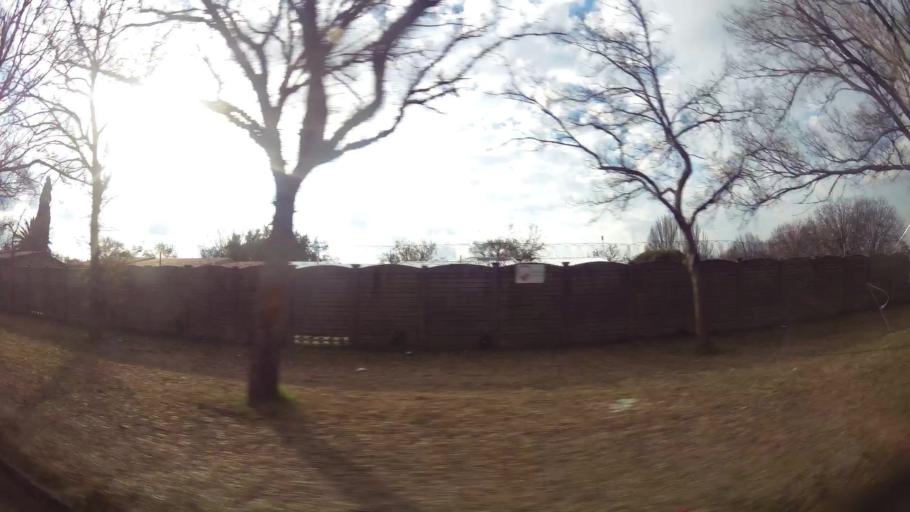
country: ZA
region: Orange Free State
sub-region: Fezile Dabi District Municipality
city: Sasolburg
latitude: -26.8180
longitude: 27.8166
